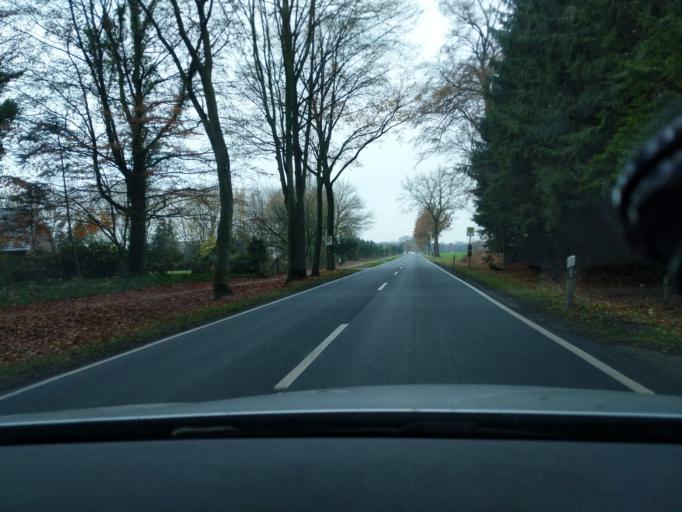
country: DE
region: Lower Saxony
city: Heeslingen
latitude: 53.3286
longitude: 9.3570
